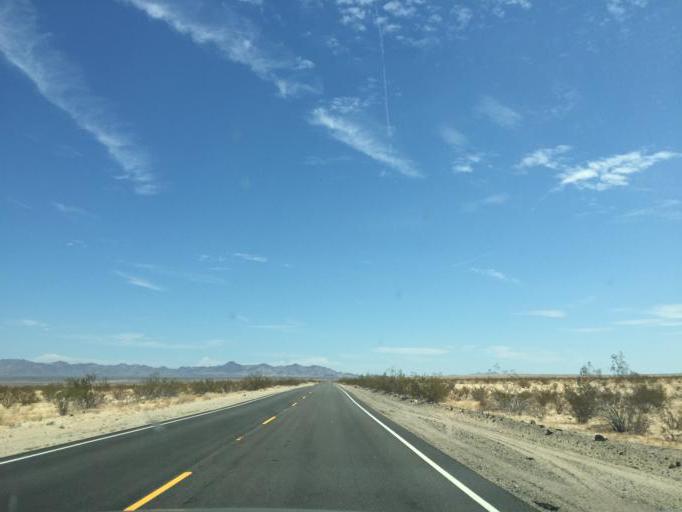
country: US
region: California
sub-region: Riverside County
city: Mesa Verde
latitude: 34.0982
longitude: -115.0175
